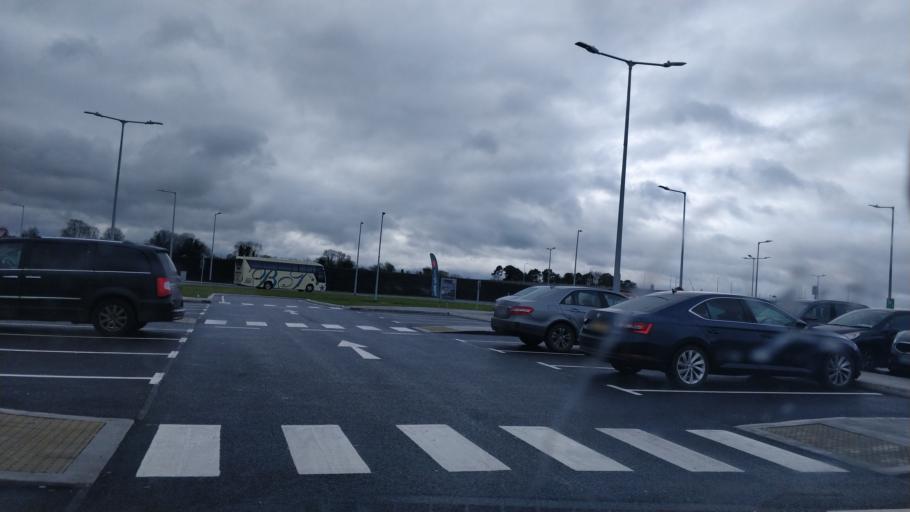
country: IE
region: Leinster
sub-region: An Iarmhi
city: Moate
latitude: 53.4007
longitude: -7.8267
